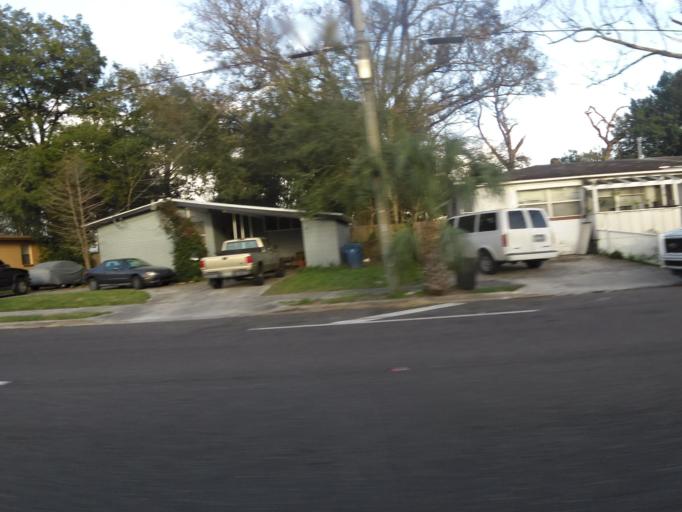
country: US
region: Florida
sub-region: Duval County
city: Jacksonville
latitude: 30.3498
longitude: -81.5895
